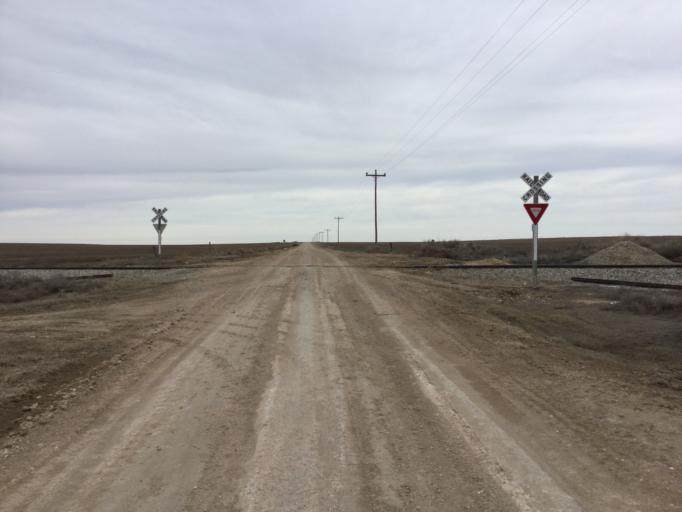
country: US
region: Kansas
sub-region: Lane County
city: Dighton
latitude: 38.4710
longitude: -100.3752
